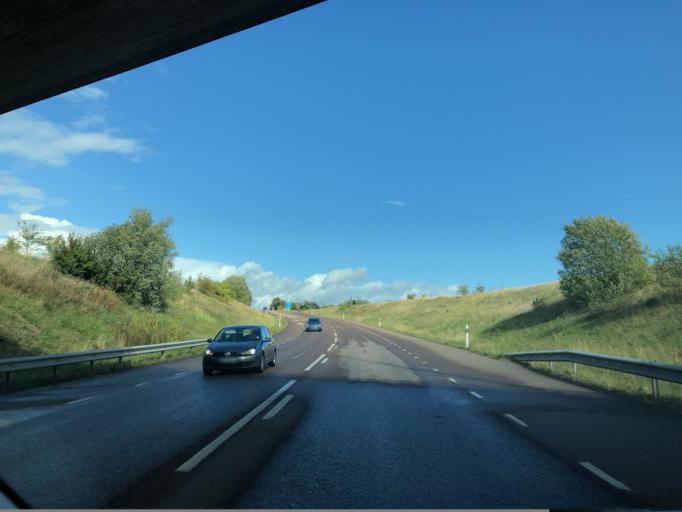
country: SE
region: Skane
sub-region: Helsingborg
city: Glumslov
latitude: 55.9188
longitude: 12.8327
